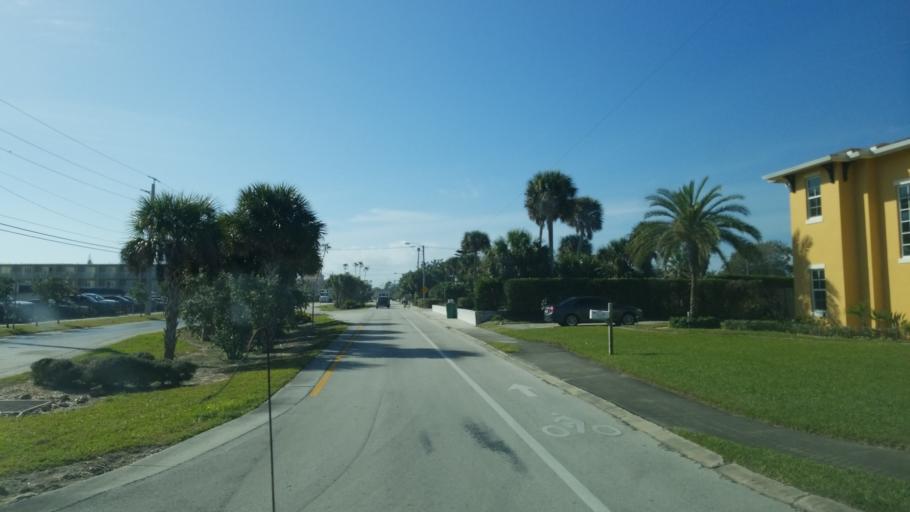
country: US
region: Florida
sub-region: Brevard County
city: Cocoa Beach
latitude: 28.3607
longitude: -80.6052
